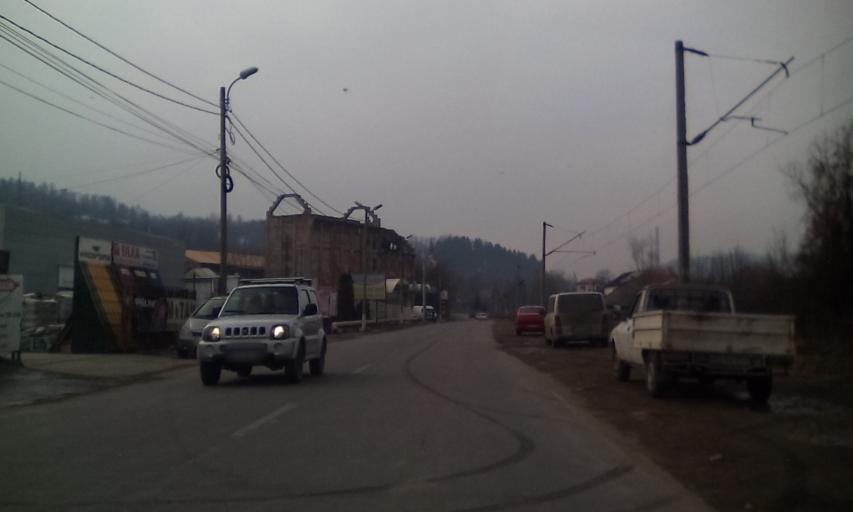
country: RO
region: Hunedoara
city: Lupeni
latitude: 45.3586
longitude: 23.2284
